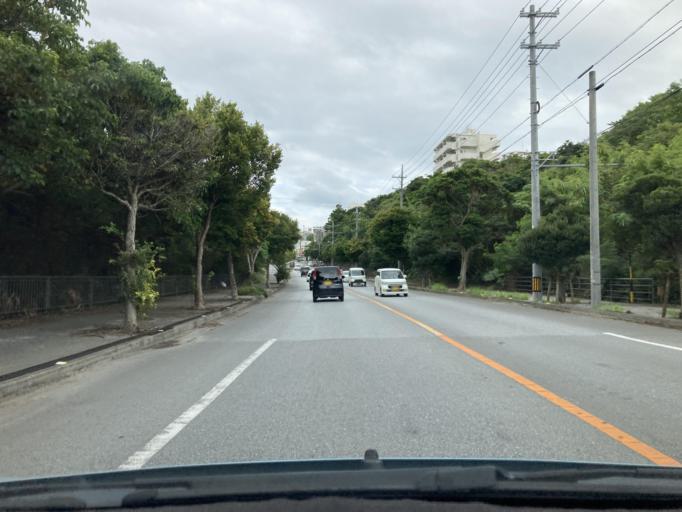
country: JP
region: Okinawa
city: Ginowan
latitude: 26.2463
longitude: 127.7588
